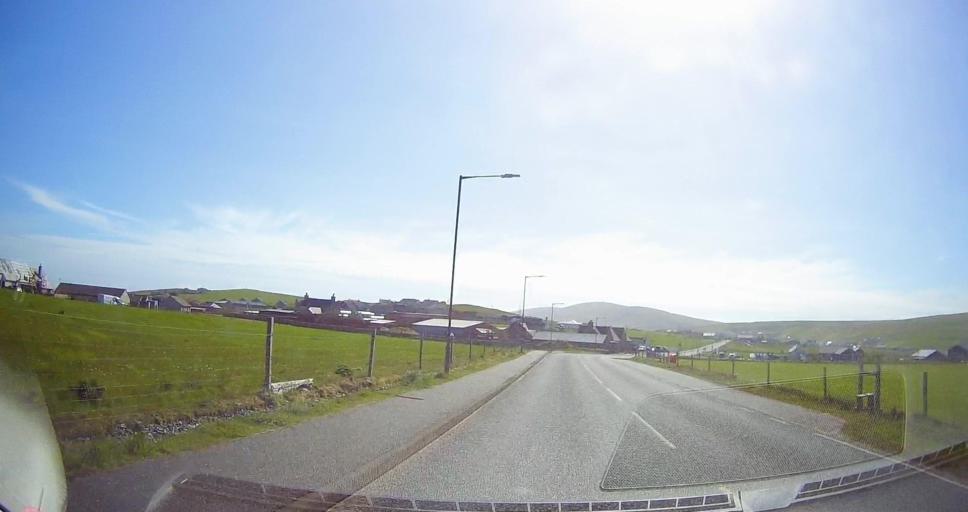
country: GB
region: Scotland
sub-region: Shetland Islands
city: Sandwick
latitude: 60.0040
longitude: -1.2327
